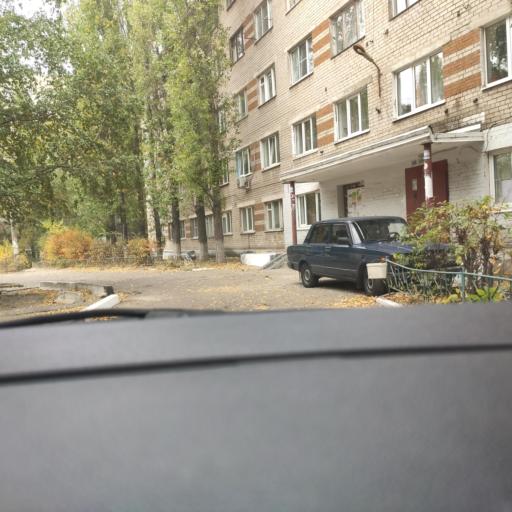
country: RU
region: Voronezj
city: Voronezh
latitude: 51.6501
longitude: 39.1294
